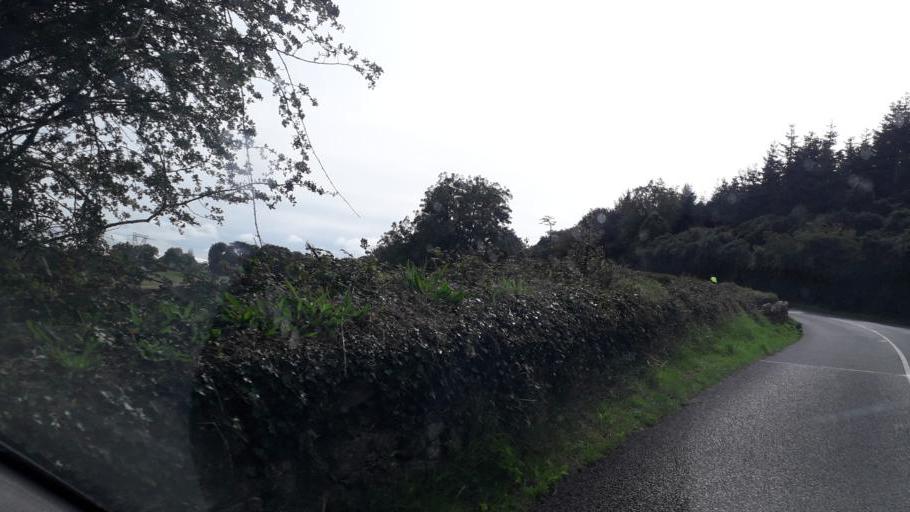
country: IE
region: Leinster
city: Sandyford
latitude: 53.2531
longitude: -6.2192
